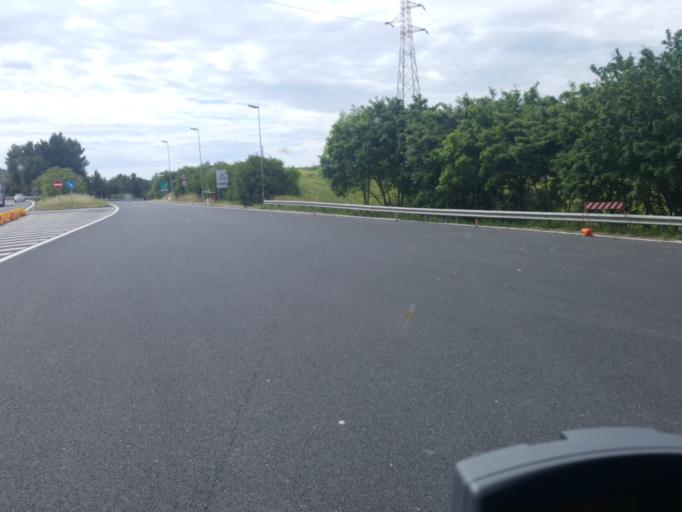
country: IT
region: Latium
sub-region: Citta metropolitana di Roma Capitale
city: Ara Nova
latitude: 41.9166
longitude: 12.2098
